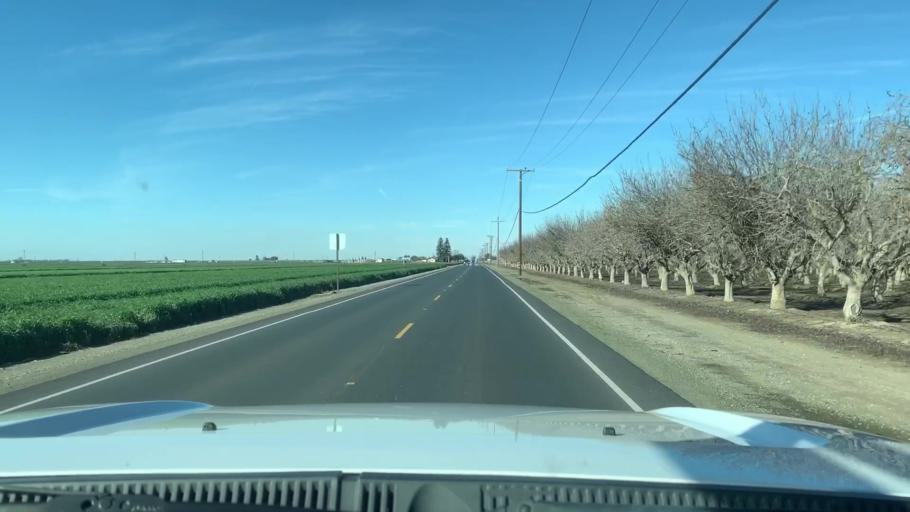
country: US
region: California
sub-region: Kings County
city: Corcoran
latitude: 36.1822
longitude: -119.4933
